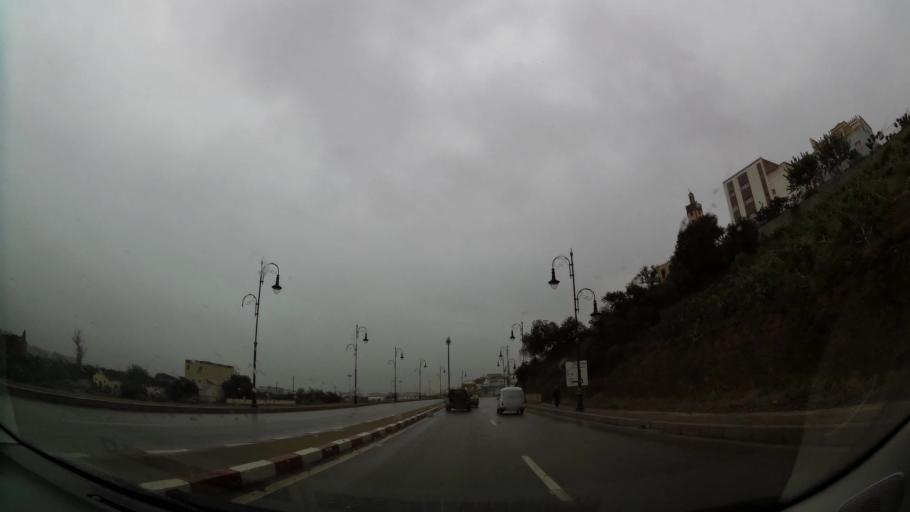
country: MA
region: Taza-Al Hoceima-Taounate
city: Imzourene
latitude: 35.1580
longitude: -3.8510
